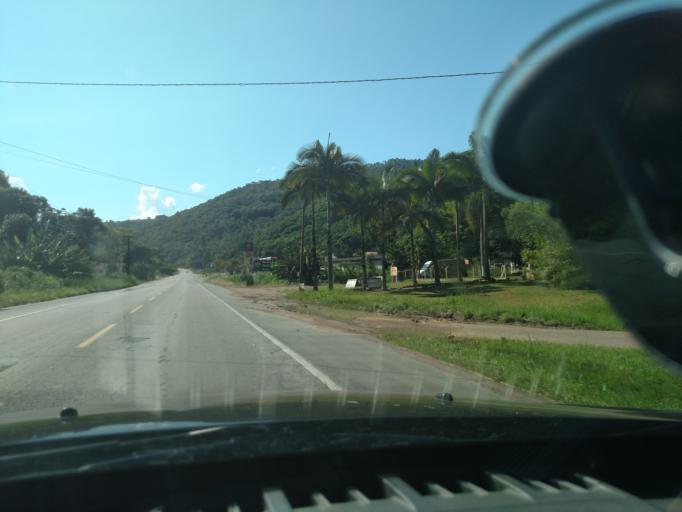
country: BR
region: Santa Catarina
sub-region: Ibirama
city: Ibirama
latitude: -27.0835
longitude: -49.4819
